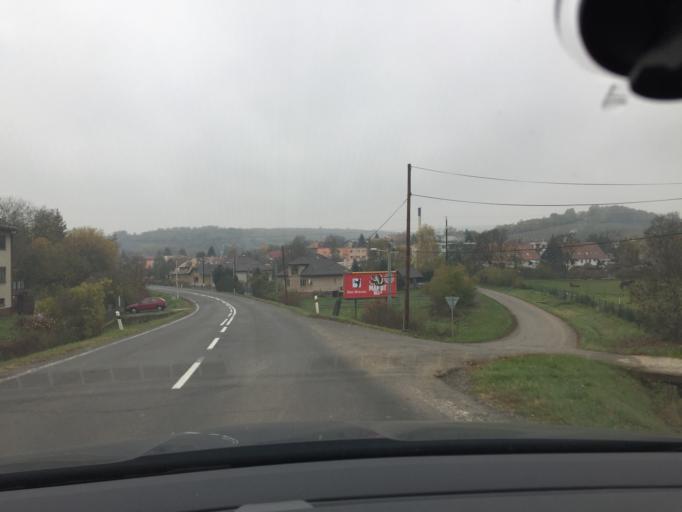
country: SK
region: Banskobystricky
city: Velky Krtis
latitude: 48.2901
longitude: 19.4913
